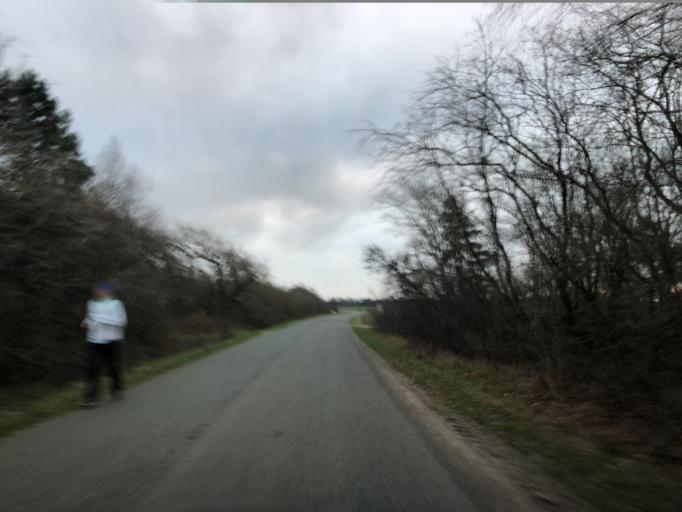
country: DK
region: Central Jutland
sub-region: Holstebro Kommune
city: Ulfborg
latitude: 56.2496
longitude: 8.2817
